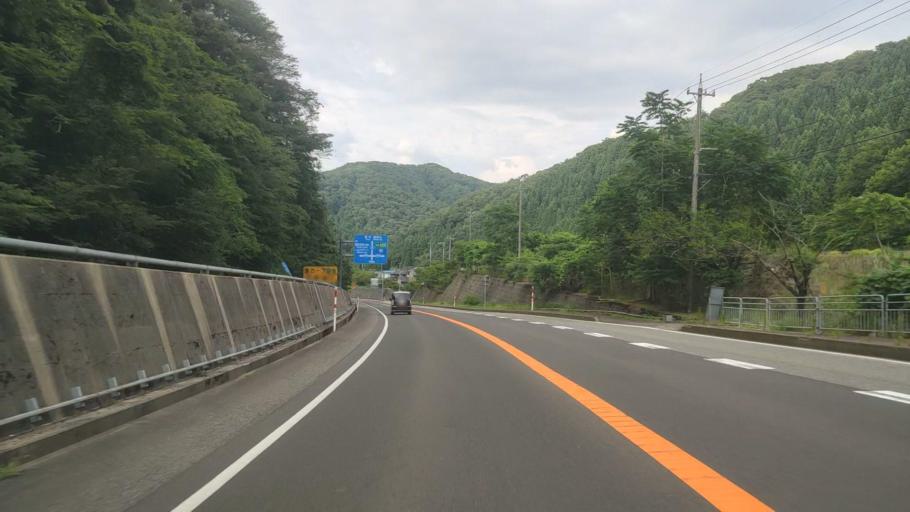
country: JP
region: Fukui
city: Takefu
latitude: 35.8124
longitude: 136.0996
